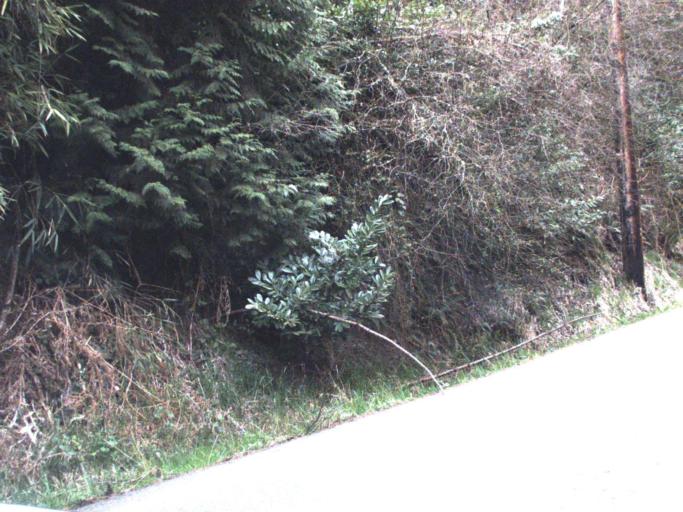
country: US
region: Washington
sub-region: King County
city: Federal Way
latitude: 47.3234
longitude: -122.3675
